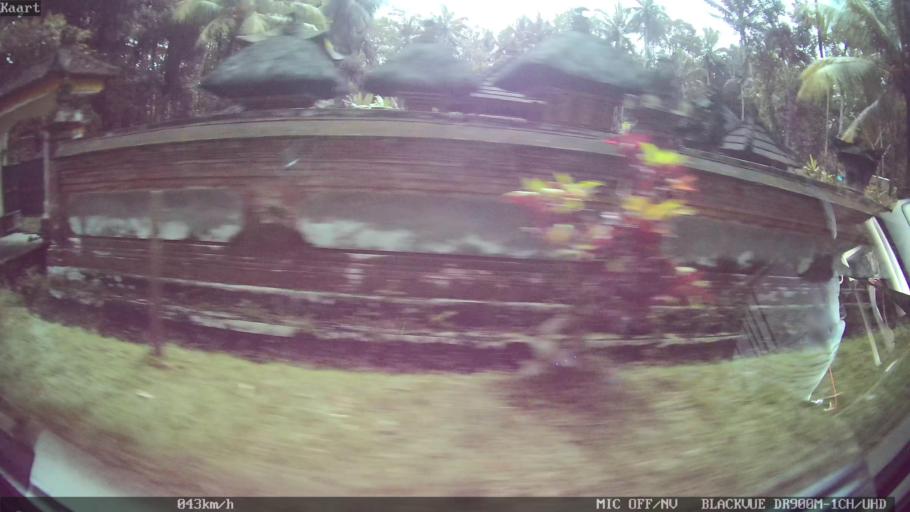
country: ID
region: Bali
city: Pegongan
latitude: -8.4742
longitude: 115.2321
